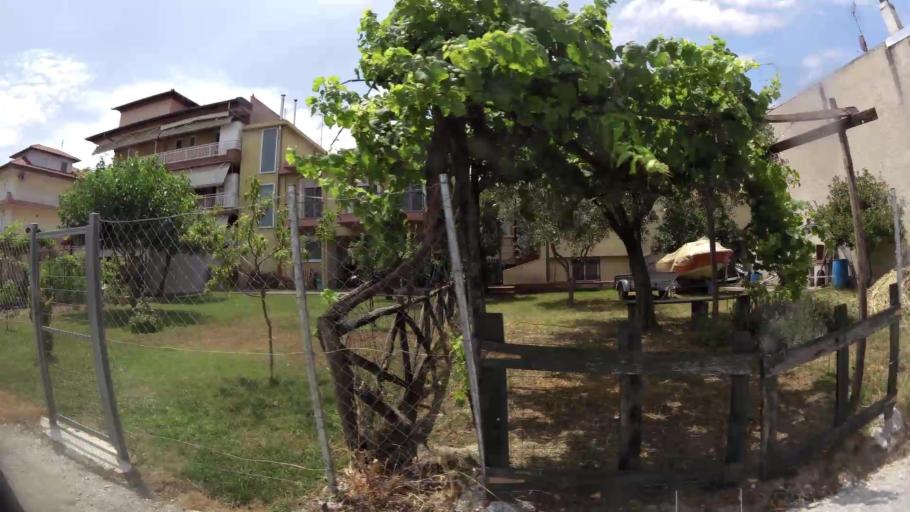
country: GR
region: Central Macedonia
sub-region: Nomos Pierias
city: Katerini
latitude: 40.2652
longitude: 22.5187
